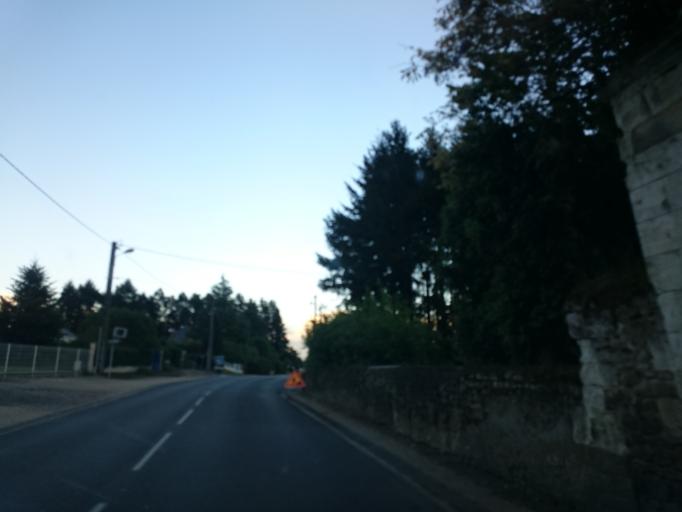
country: FR
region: Centre
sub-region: Departement d'Indre-et-Loire
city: Civray-de-Touraine
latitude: 47.3328
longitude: 1.0524
